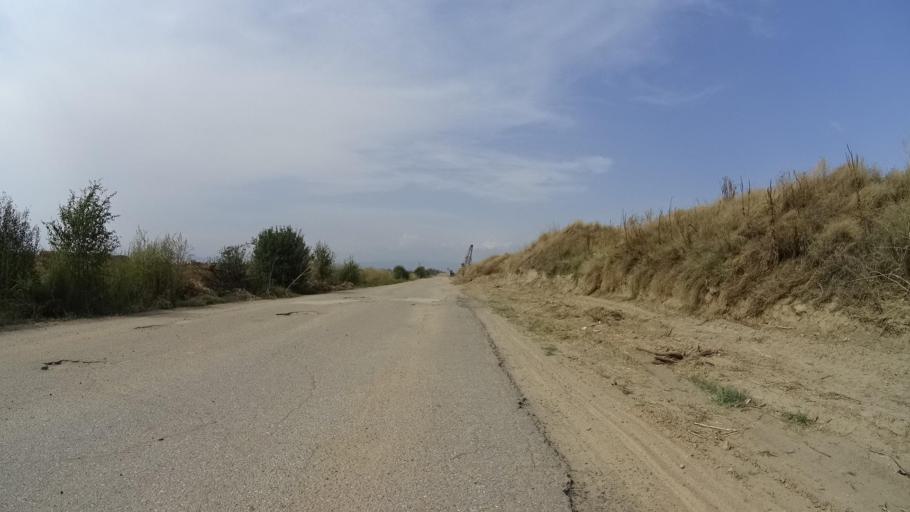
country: BG
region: Plovdiv
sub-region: Obshtina Kaloyanovo
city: Kaloyanovo
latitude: 42.3104
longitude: 24.7997
